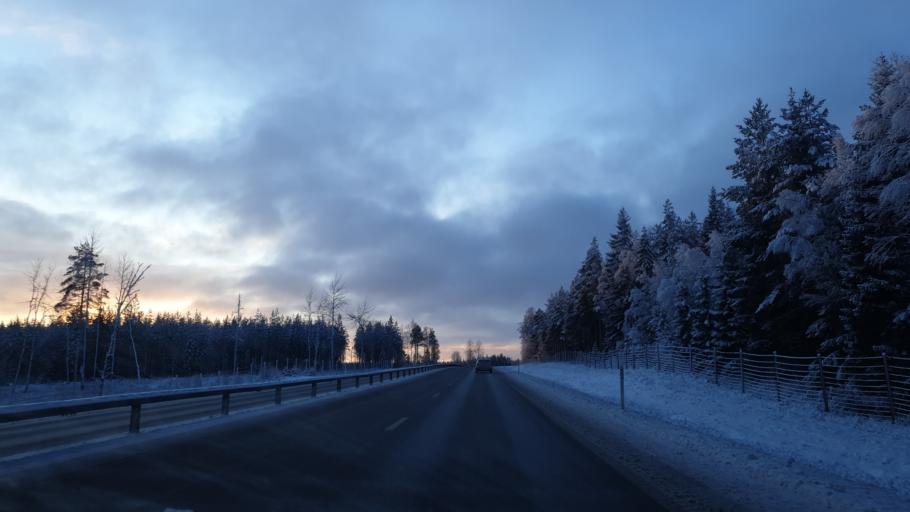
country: SE
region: Vaesterbotten
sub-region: Umea Kommun
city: Hoernefors
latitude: 63.6208
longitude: 19.8404
